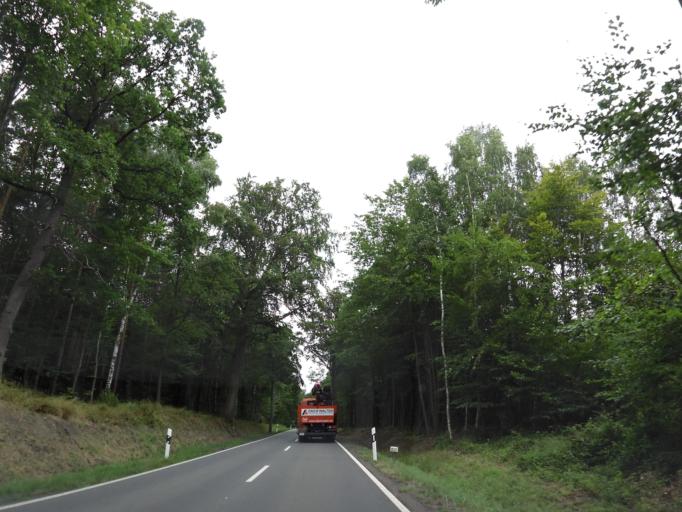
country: DE
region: Thuringia
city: Weissenborn
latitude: 50.9496
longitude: 11.8639
